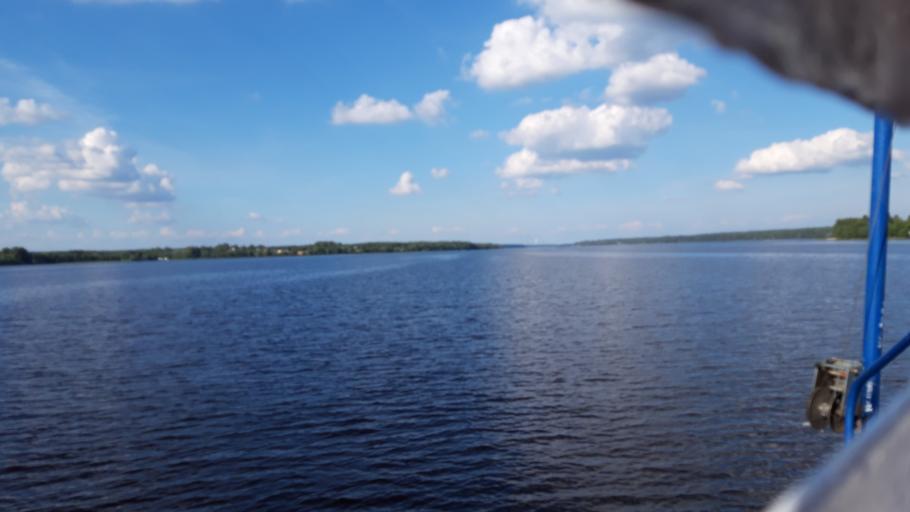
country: RU
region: Tverskaya
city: Konakovo
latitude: 56.6616
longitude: 36.6483
